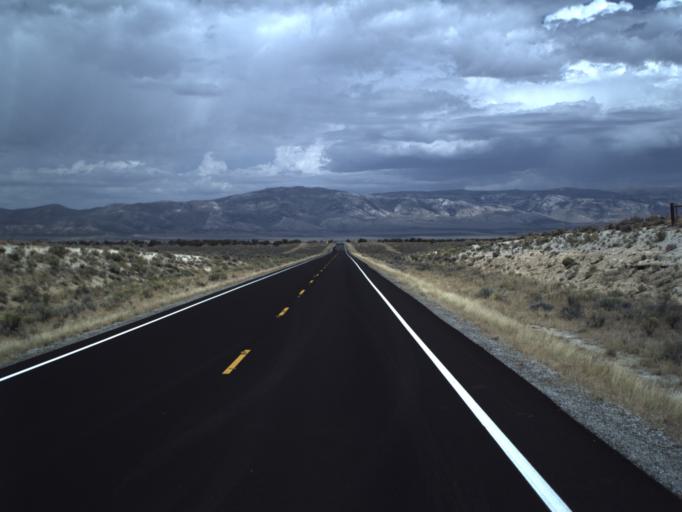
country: US
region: Idaho
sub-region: Cassia County
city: Burley
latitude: 41.7134
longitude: -113.5291
